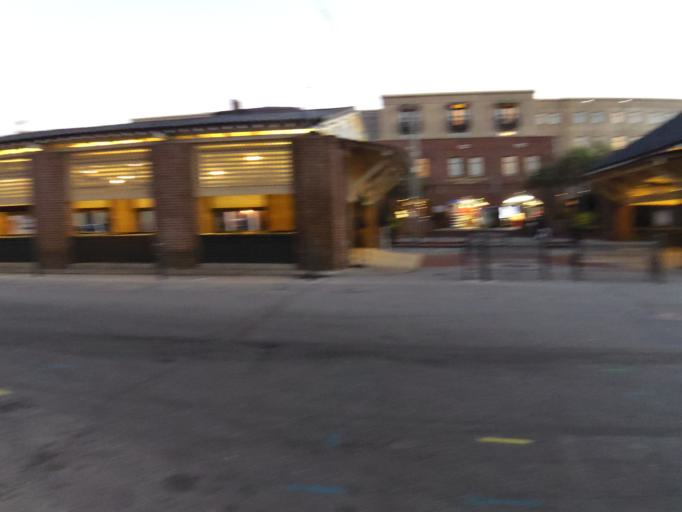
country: US
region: South Carolina
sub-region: Charleston County
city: Charleston
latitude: 32.7811
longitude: -79.9290
